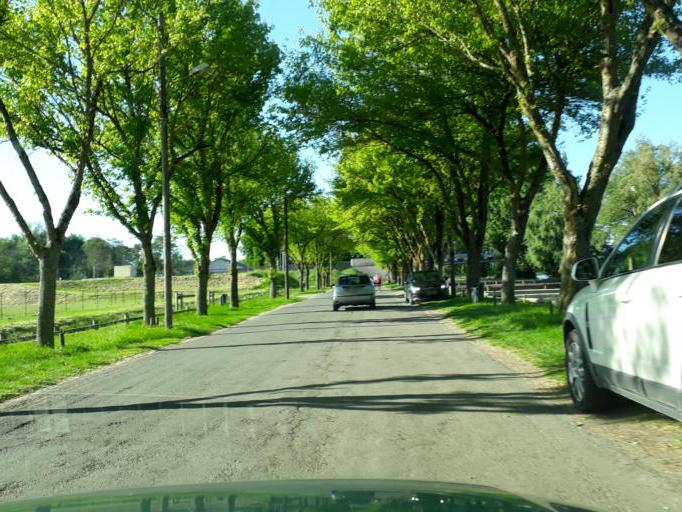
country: FR
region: Bourgogne
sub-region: Departement de la Nievre
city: Cosne-Cours-sur-Loire
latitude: 47.4098
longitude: 2.9178
